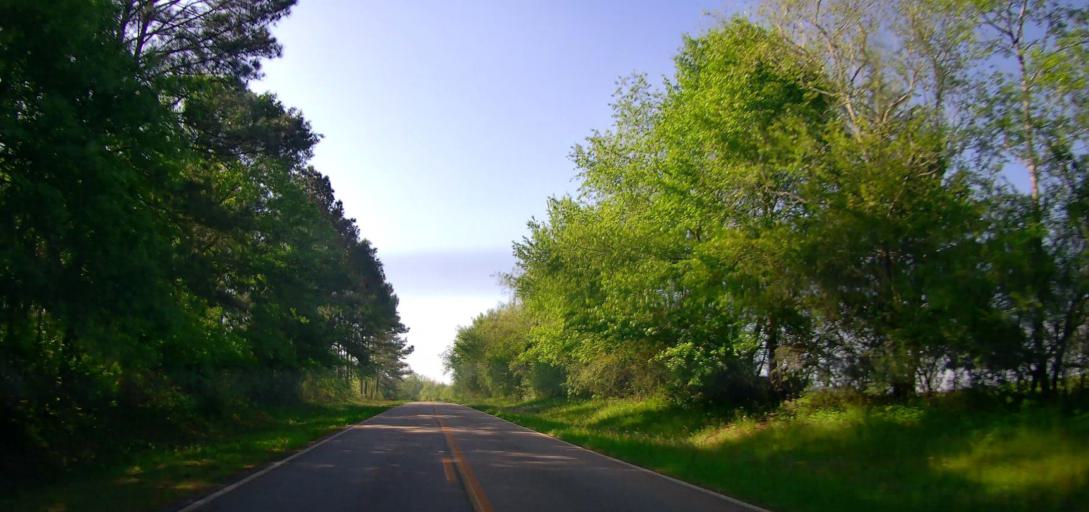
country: US
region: Georgia
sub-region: Morgan County
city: Madison
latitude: 33.5303
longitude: -83.5114
